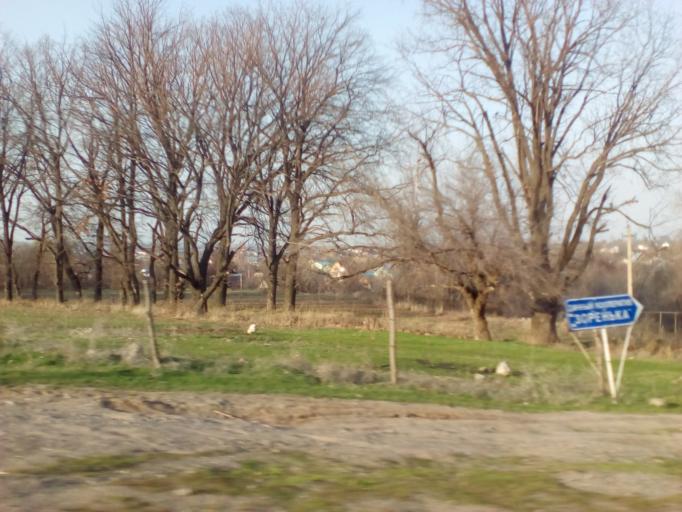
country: KZ
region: Almaty Oblysy
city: Burunday
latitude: 43.1652
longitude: 76.5479
